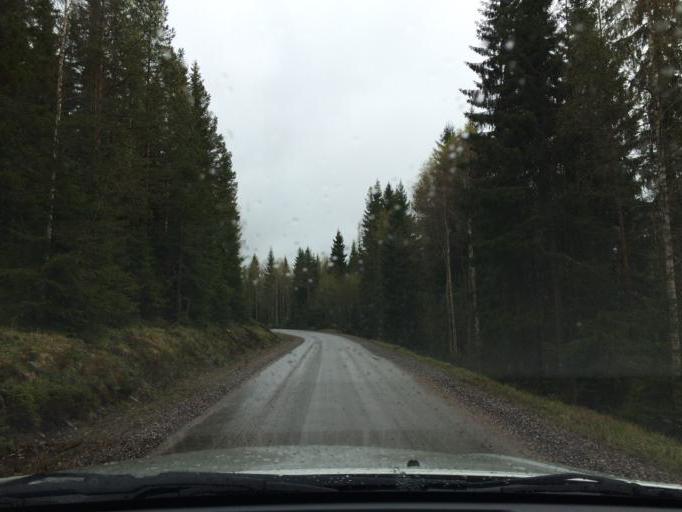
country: SE
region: Dalarna
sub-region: Ludvika Kommun
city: Abborrberget
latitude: 60.0397
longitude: 14.6410
